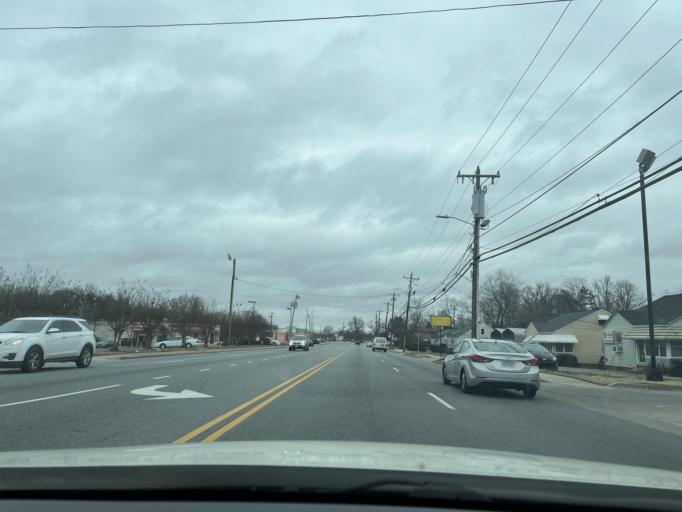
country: US
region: North Carolina
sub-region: Guilford County
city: Greensboro
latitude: 36.0156
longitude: -79.8043
